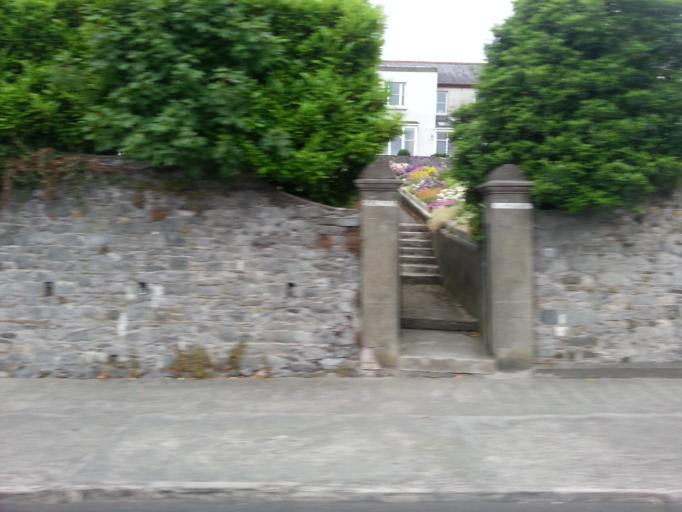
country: IE
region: Leinster
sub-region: Kilkenny
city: Kilkenny
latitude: 52.6526
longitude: -7.2413
